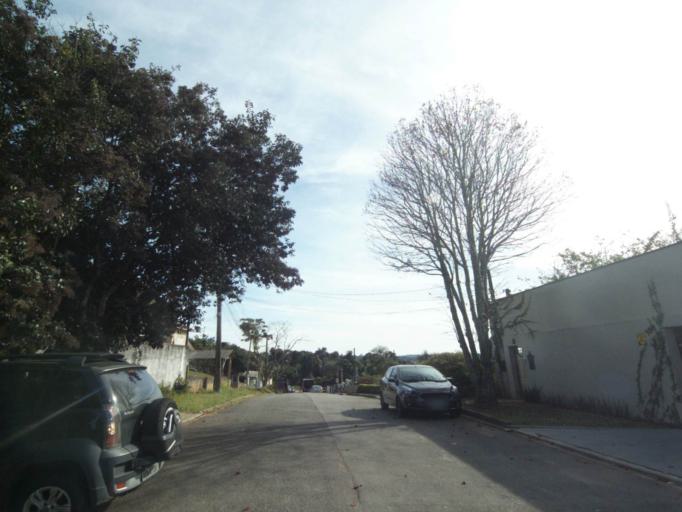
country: BR
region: Parana
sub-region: Curitiba
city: Curitiba
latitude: -25.4184
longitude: -49.3006
